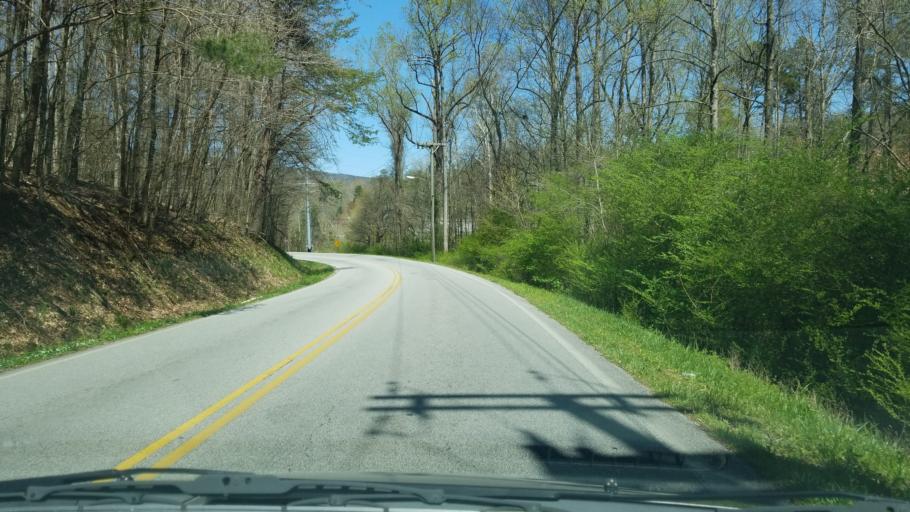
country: US
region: Tennessee
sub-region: Hamilton County
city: Middle Valley
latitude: 35.2092
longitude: -85.2129
